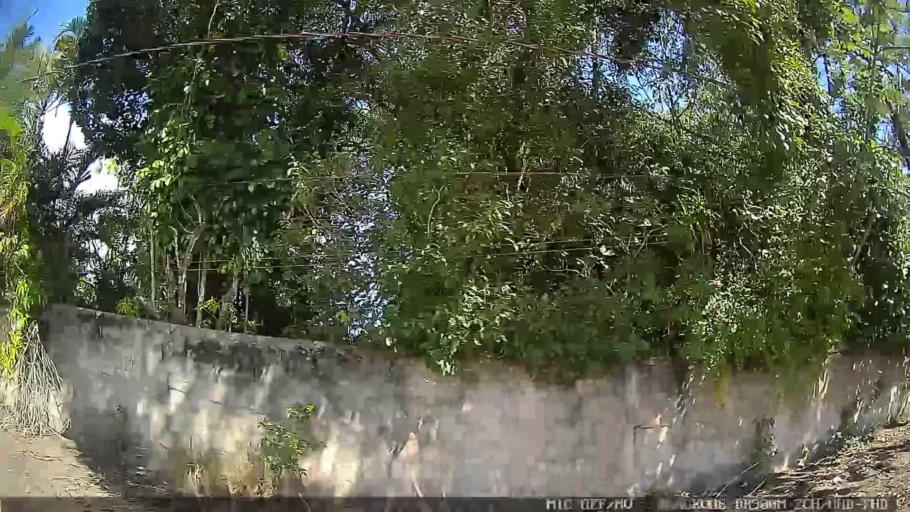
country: BR
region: Sao Paulo
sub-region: Itanhaem
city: Itanhaem
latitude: -24.2194
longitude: -46.8598
